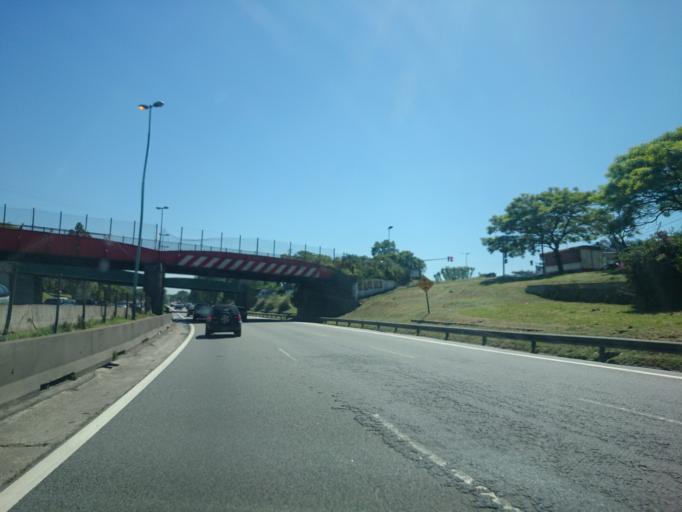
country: AR
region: Buenos Aires F.D.
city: Villa Lugano
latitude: -34.6821
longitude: -58.4810
